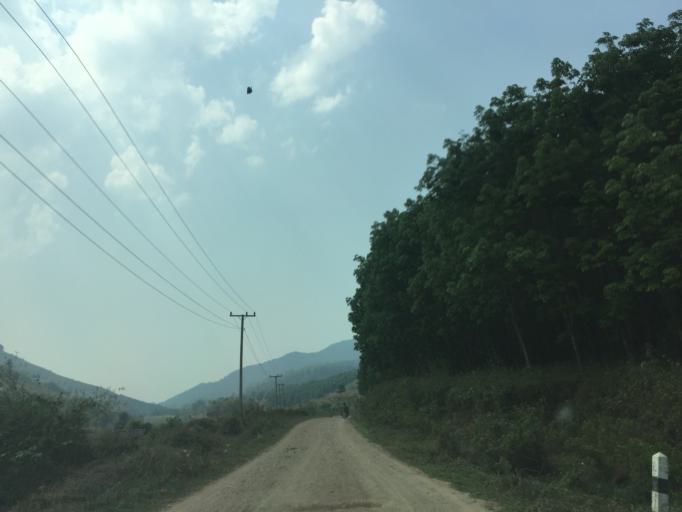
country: TH
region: Nan
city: Song Khwae
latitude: 19.7327
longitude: 100.7286
